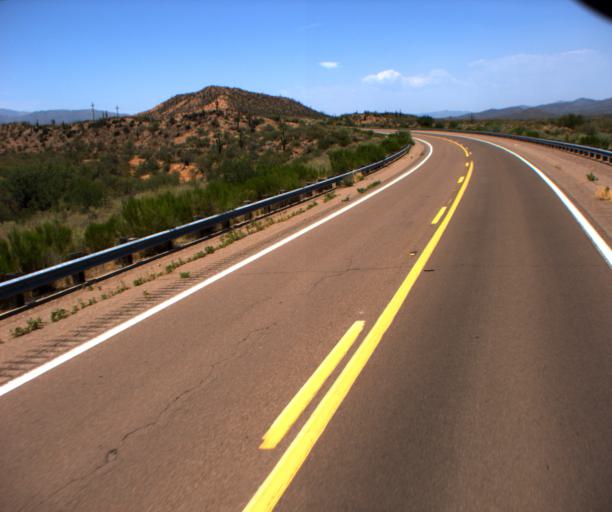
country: US
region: Arizona
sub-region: Gila County
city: Tonto Basin
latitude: 33.8944
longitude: -111.3100
